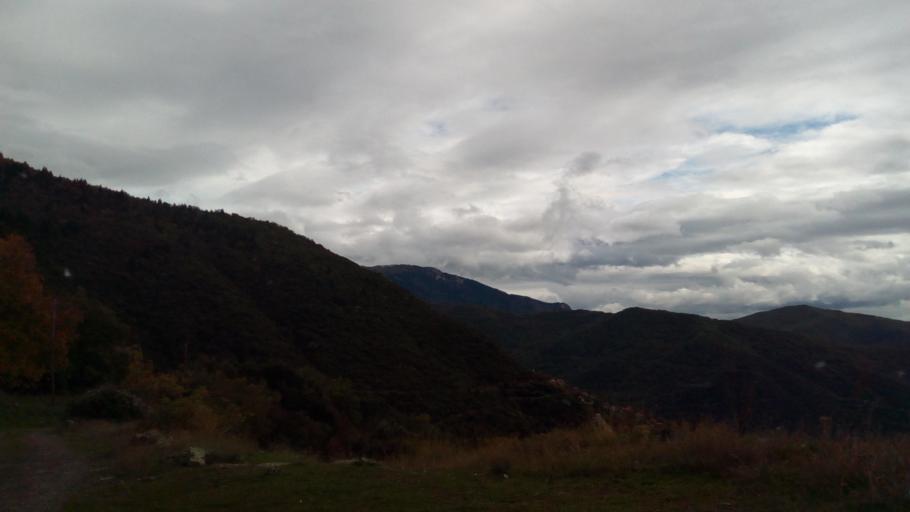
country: GR
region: West Greece
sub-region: Nomos Aitolias kai Akarnanias
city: Nafpaktos
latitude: 38.5641
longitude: 21.9598
